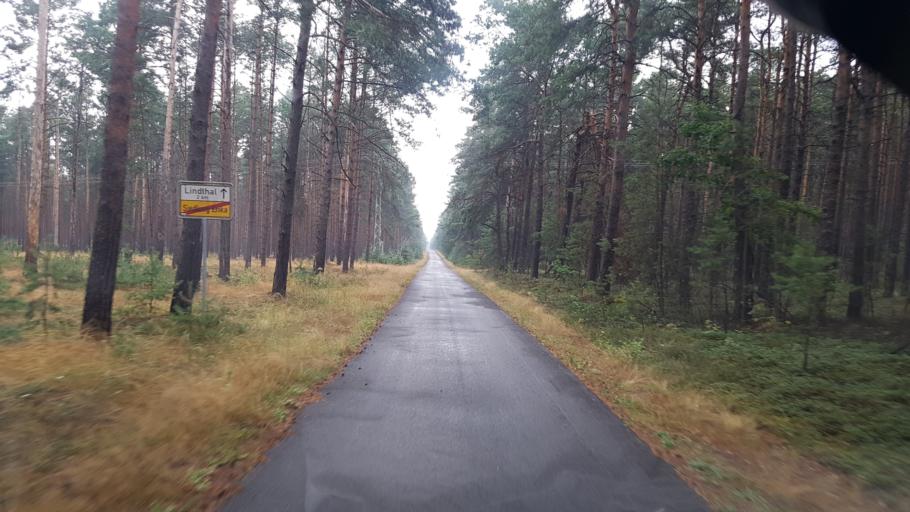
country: DE
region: Brandenburg
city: Finsterwalde
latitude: 51.6460
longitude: 13.7850
